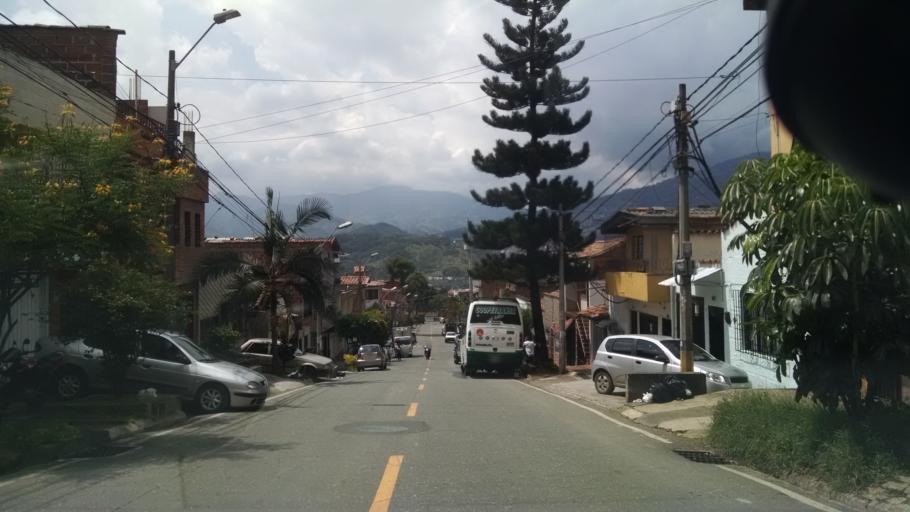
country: CO
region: Antioquia
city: Medellin
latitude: 6.2649
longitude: -75.5576
